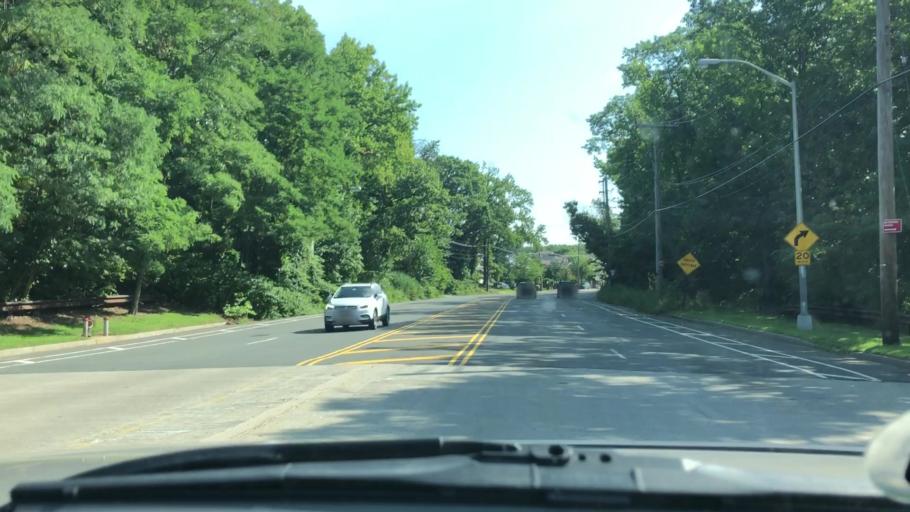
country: US
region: New Jersey
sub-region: Middlesex County
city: Perth Amboy
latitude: 40.5178
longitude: -74.2009
